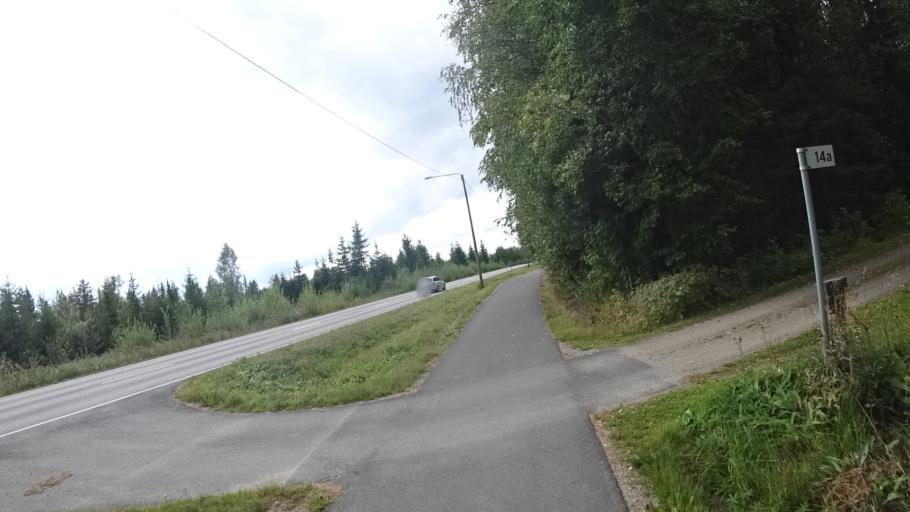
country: FI
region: North Karelia
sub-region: Joensuu
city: Ilomantsi
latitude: 62.6534
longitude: 30.9607
